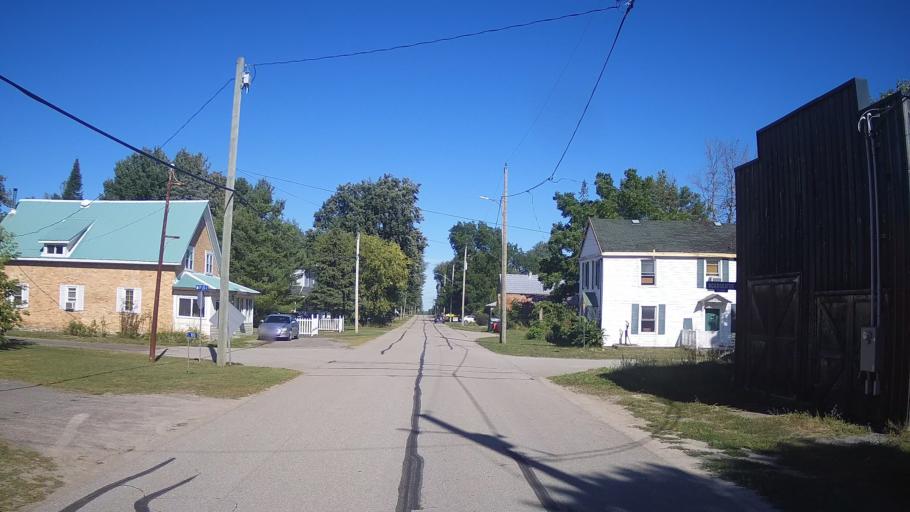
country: CA
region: Ontario
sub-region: Lanark County
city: Smiths Falls
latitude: 44.8377
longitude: -75.8861
